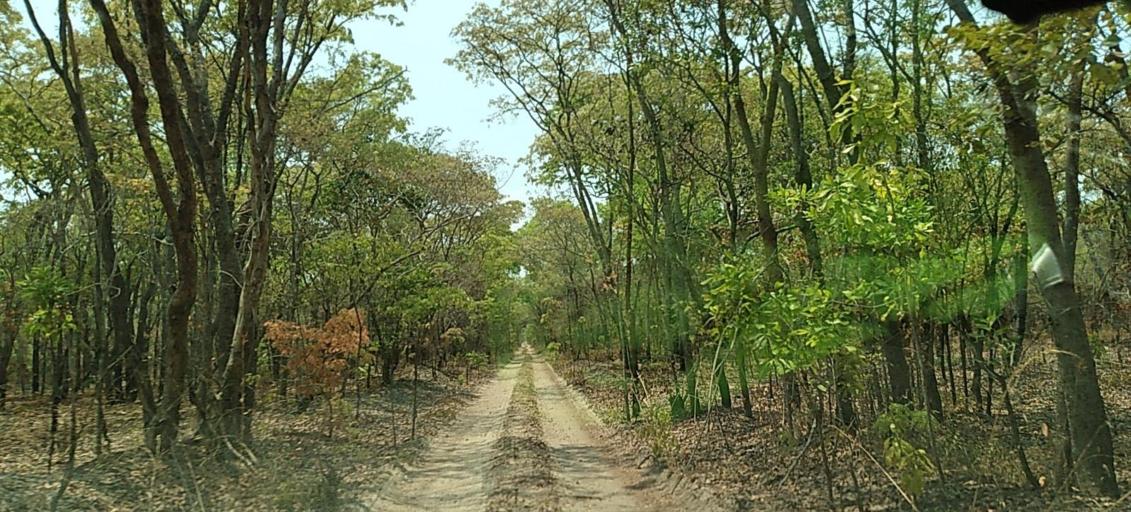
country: ZM
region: North-Western
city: Kabompo
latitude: -13.6565
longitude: 24.4641
